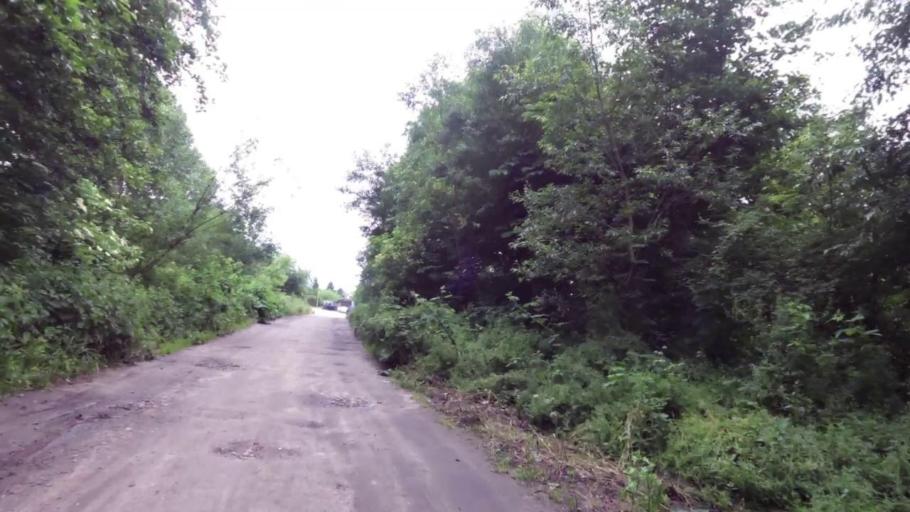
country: PL
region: West Pomeranian Voivodeship
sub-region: Szczecin
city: Szczecin
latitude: 53.4032
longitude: 14.6721
